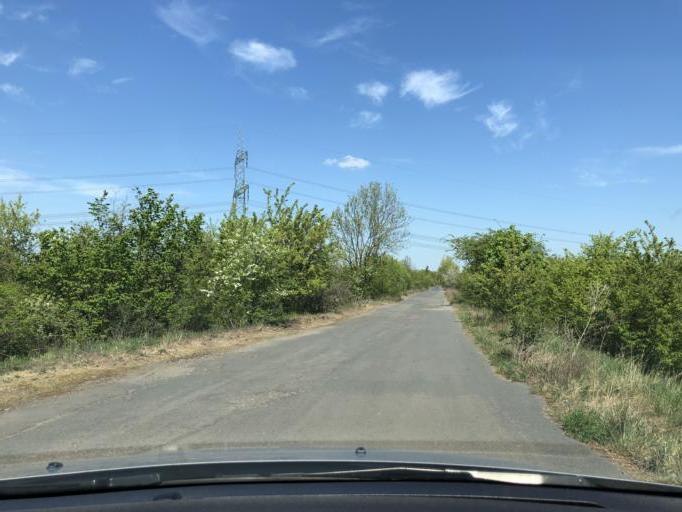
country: DE
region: Saxony-Anhalt
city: Dieskau
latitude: 51.4453
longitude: 11.9993
